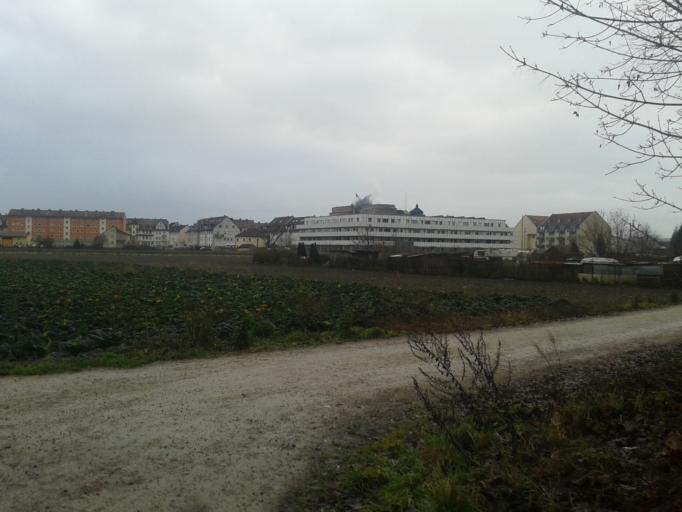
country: DE
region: Bavaria
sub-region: Upper Franconia
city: Bamberg
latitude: 49.9091
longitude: 10.8952
